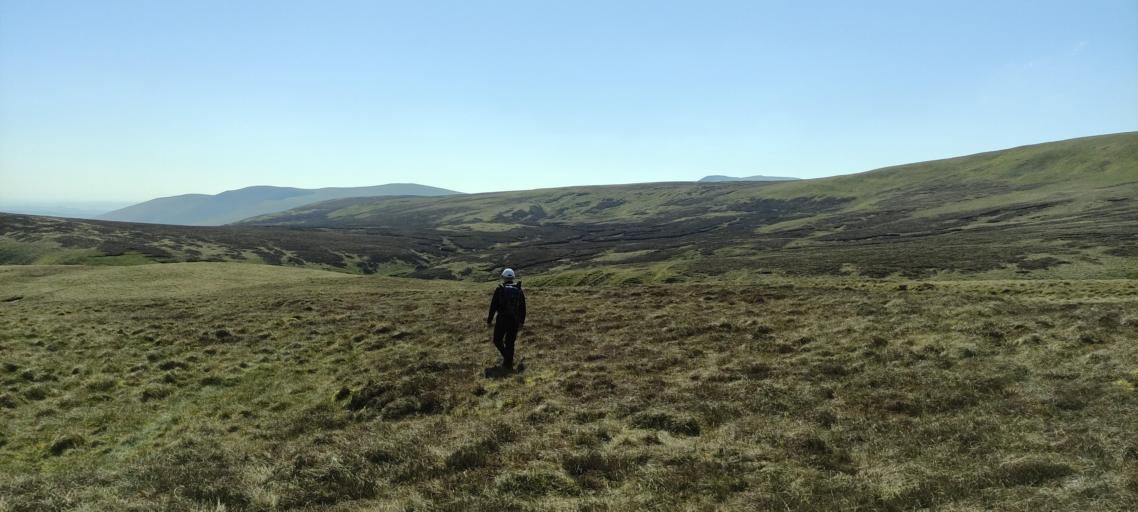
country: GB
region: England
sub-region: Cumbria
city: Keswick
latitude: 54.6964
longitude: -3.0931
